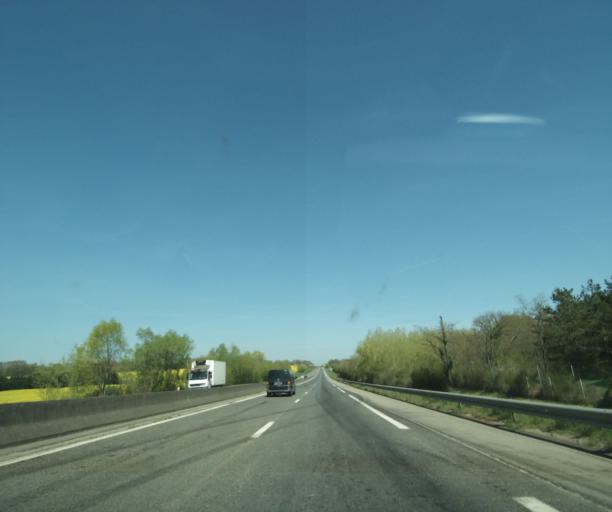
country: FR
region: Auvergne
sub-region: Departement de l'Allier
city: Yzeure
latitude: 46.5583
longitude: 3.3874
